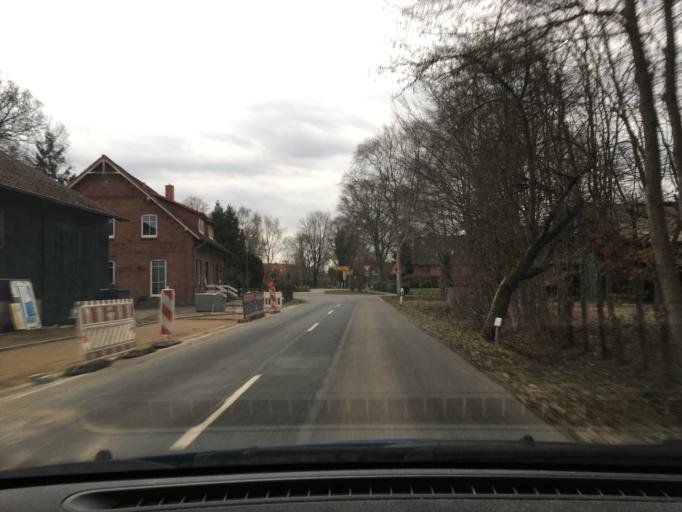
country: DE
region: Lower Saxony
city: Handorf
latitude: 53.3682
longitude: 10.3337
